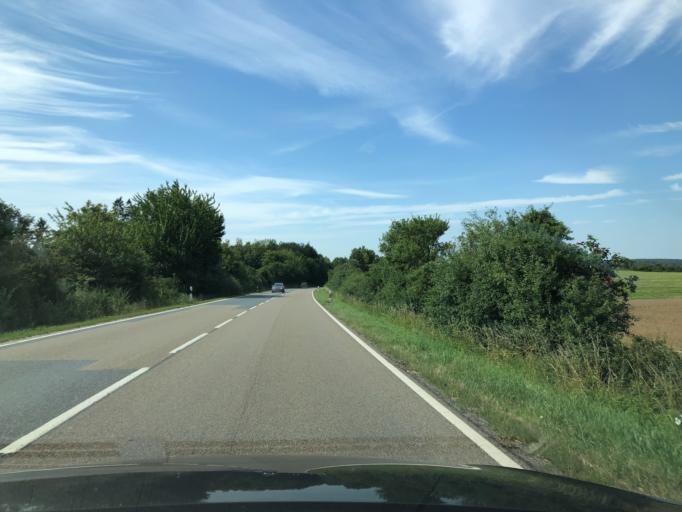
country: DE
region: Bavaria
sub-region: Upper Bavaria
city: Denkendorf
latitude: 48.9383
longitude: 11.4692
